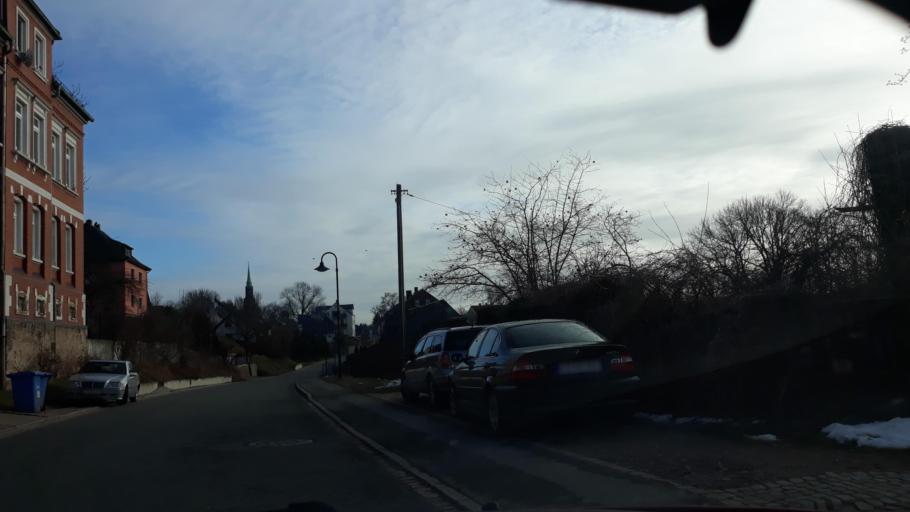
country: DE
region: Saxony
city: Reinsdorf
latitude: 50.7022
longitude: 12.5517
